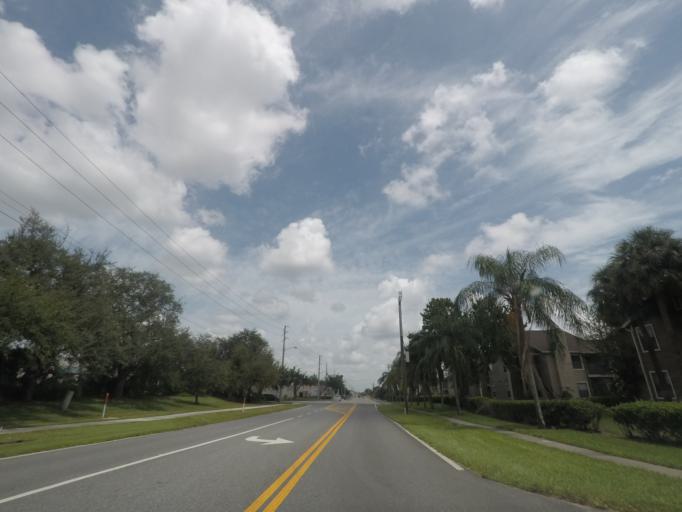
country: US
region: Florida
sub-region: Osceola County
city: Kissimmee
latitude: 28.2991
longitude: -81.4368
